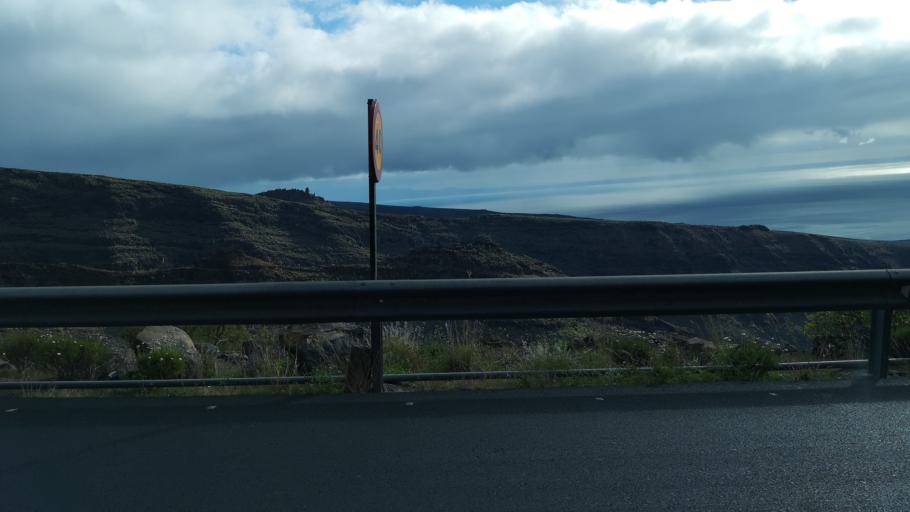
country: ES
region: Canary Islands
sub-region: Provincia de Santa Cruz de Tenerife
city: Alajero
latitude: 28.0582
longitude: -17.2025
